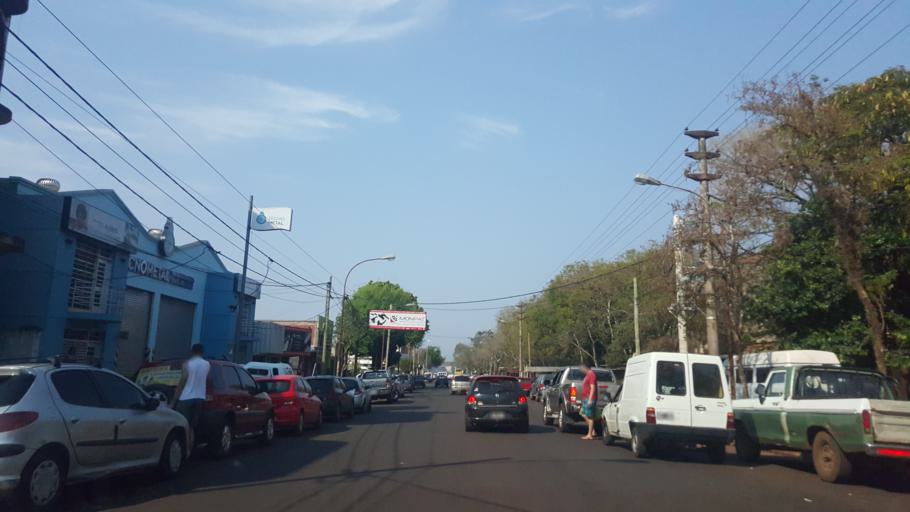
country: AR
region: Misiones
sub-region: Departamento de Capital
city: Posadas
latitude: -27.3949
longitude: -55.9052
